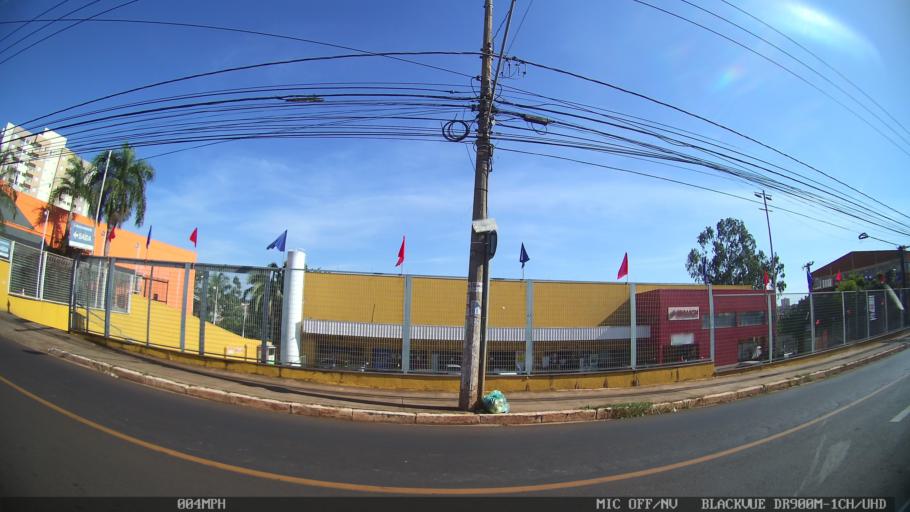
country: BR
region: Sao Paulo
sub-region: Ribeirao Preto
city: Ribeirao Preto
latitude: -21.1817
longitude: -47.7746
